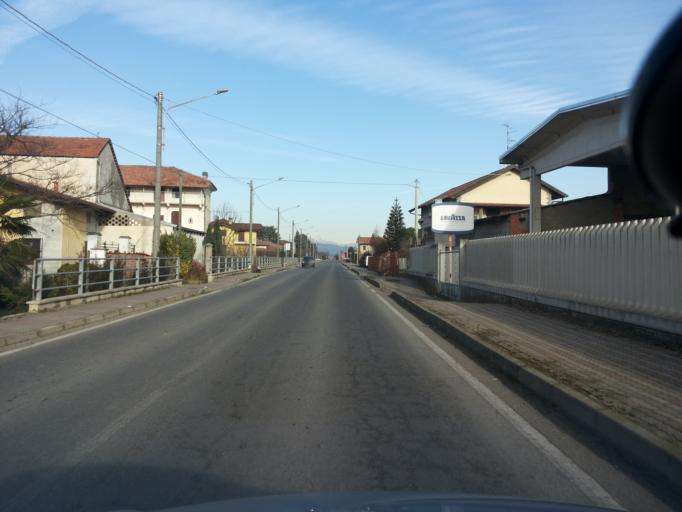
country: IT
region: Piedmont
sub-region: Provincia di Vercelli
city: Ghislarengo
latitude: 45.5312
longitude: 8.3859
